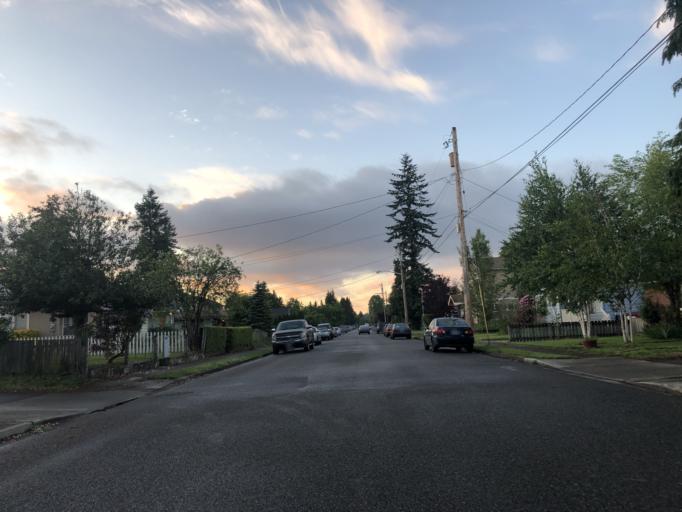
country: US
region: Washington
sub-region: King County
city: Auburn
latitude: 47.3084
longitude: -122.2095
